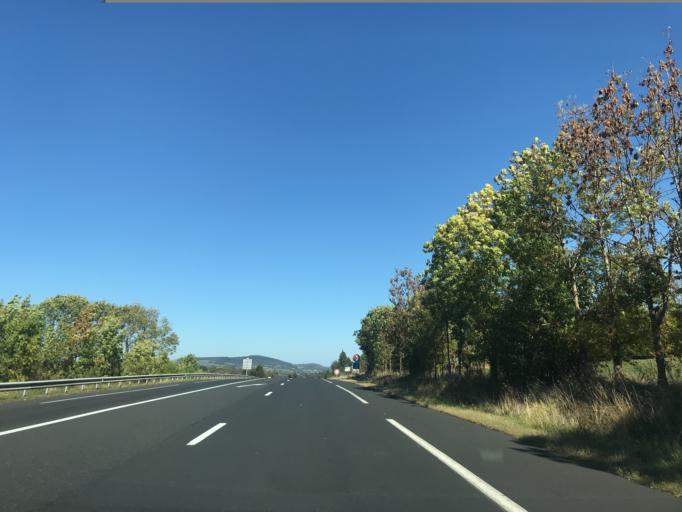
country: FR
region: Auvergne
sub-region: Departement du Puy-de-Dome
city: Gelles
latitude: 45.6792
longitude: 2.7977
